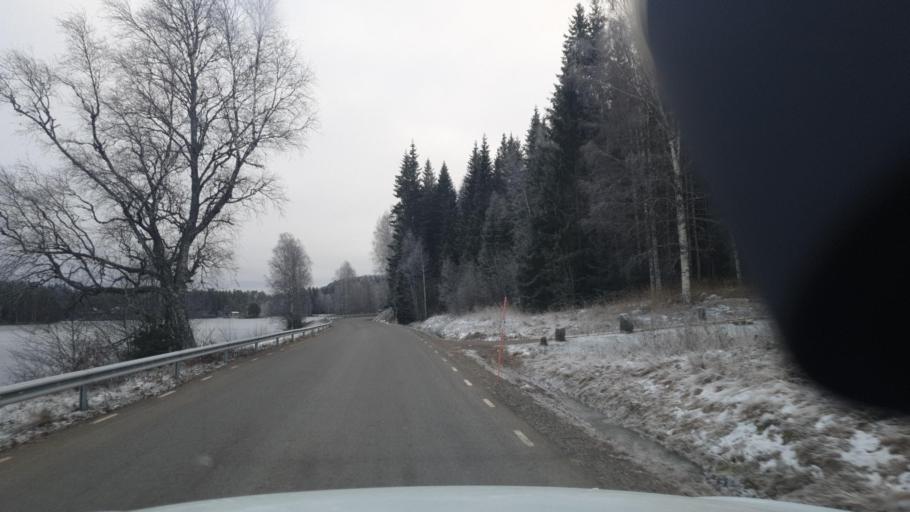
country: SE
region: Vaermland
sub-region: Eda Kommun
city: Charlottenberg
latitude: 60.0252
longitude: 12.6144
